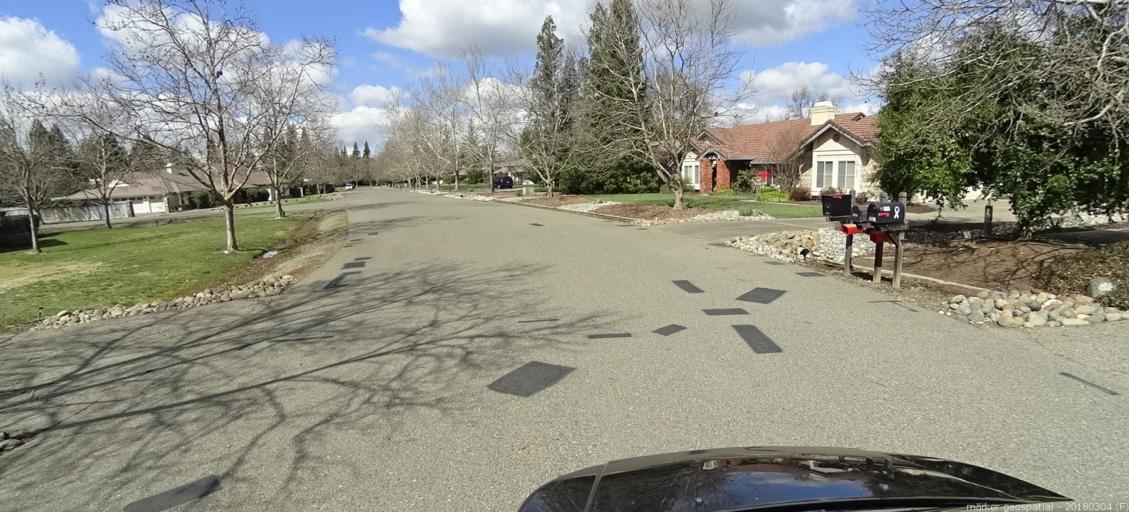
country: US
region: California
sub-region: Sacramento County
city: Vineyard
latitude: 38.4560
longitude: -121.3081
